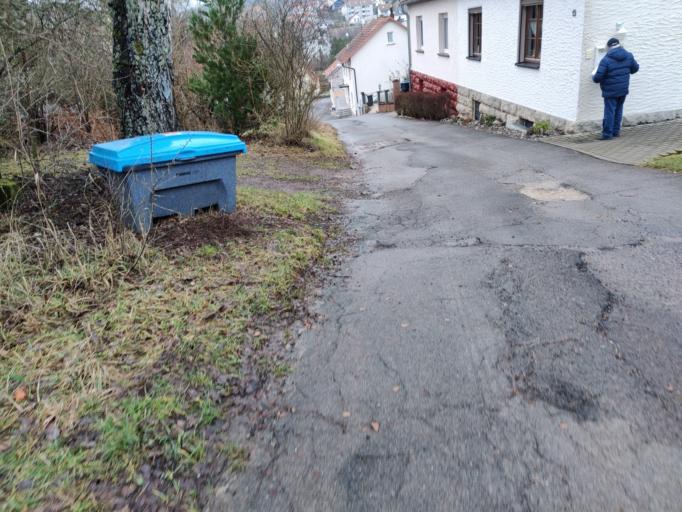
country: DE
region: Bavaria
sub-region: Regierungsbezirk Unterfranken
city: Bad Kissingen
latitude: 50.2028
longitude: 10.0966
